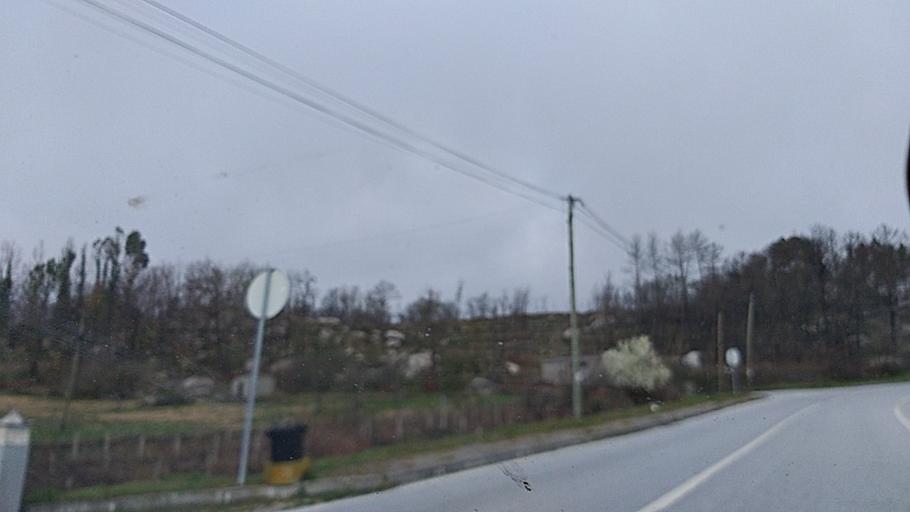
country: PT
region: Guarda
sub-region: Fornos de Algodres
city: Fornos de Algodres
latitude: 40.6774
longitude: -7.4722
